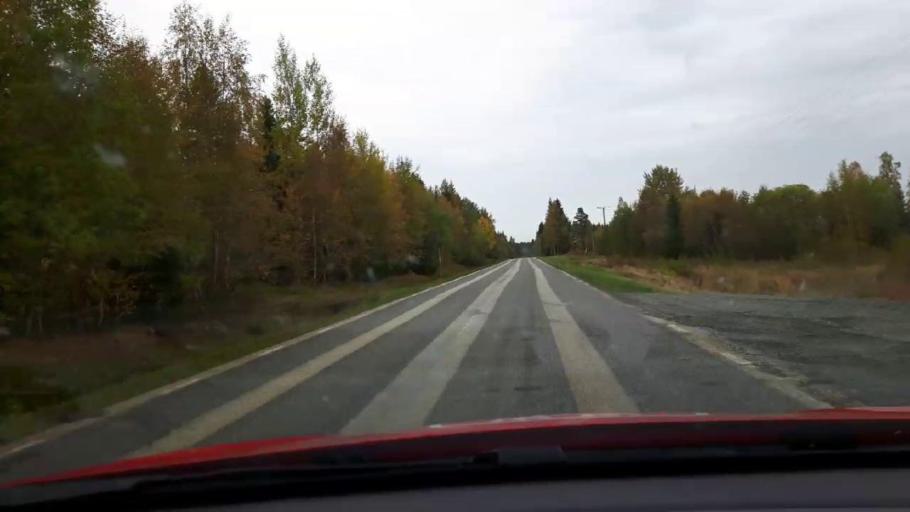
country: SE
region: Jaemtland
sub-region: Bergs Kommun
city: Hoverberg
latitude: 62.8674
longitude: 14.3734
